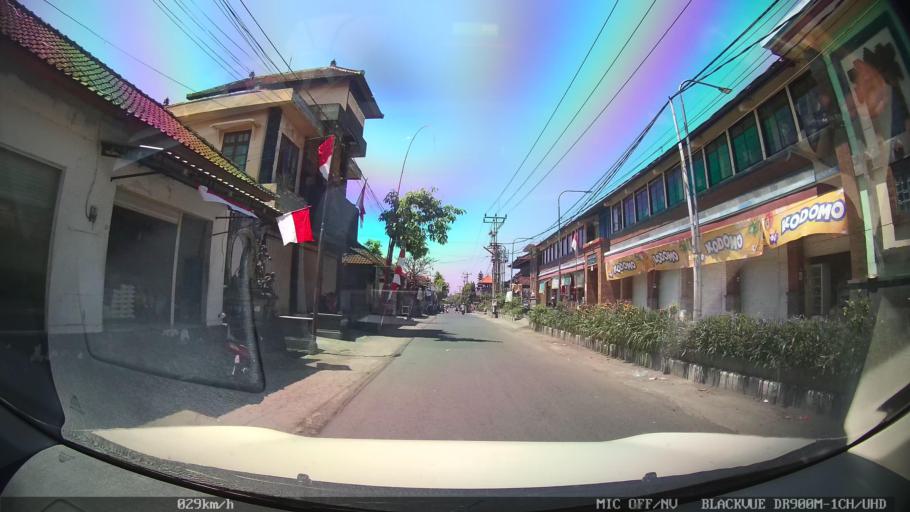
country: ID
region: Bali
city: Banjar Pasekan
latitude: -8.5764
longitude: 115.3243
